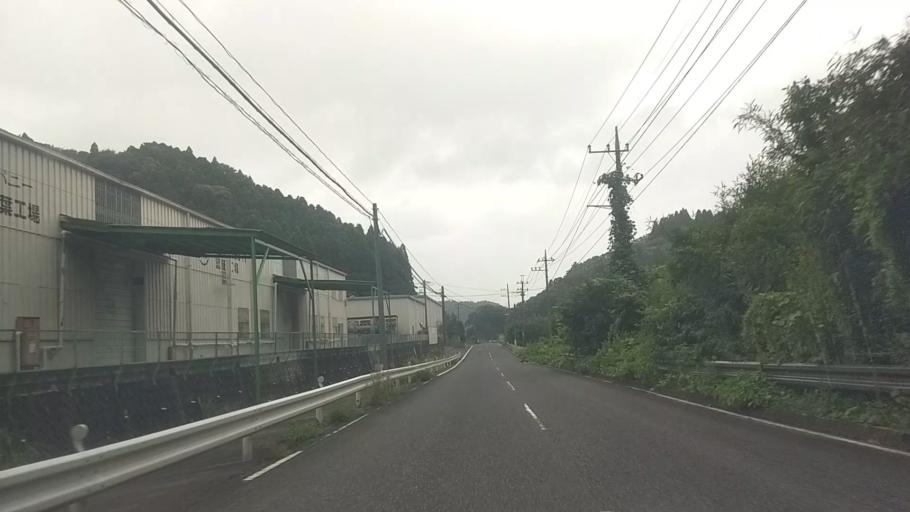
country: JP
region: Chiba
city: Katsuura
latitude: 35.2512
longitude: 140.2441
